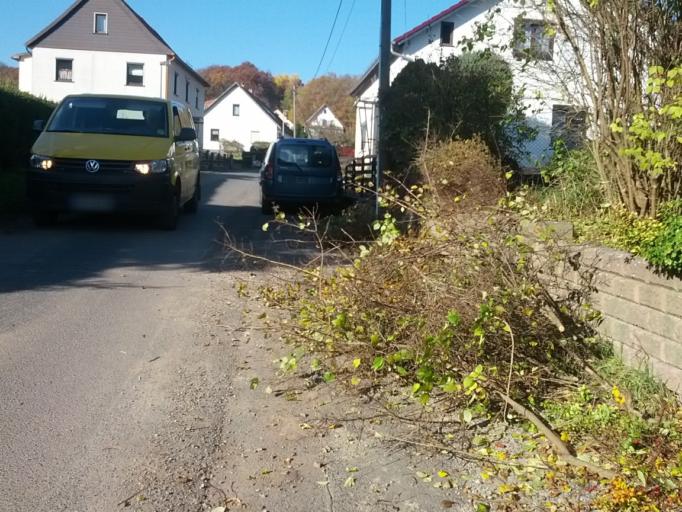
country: DE
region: Thuringia
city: Thal
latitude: 50.9240
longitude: 10.3763
